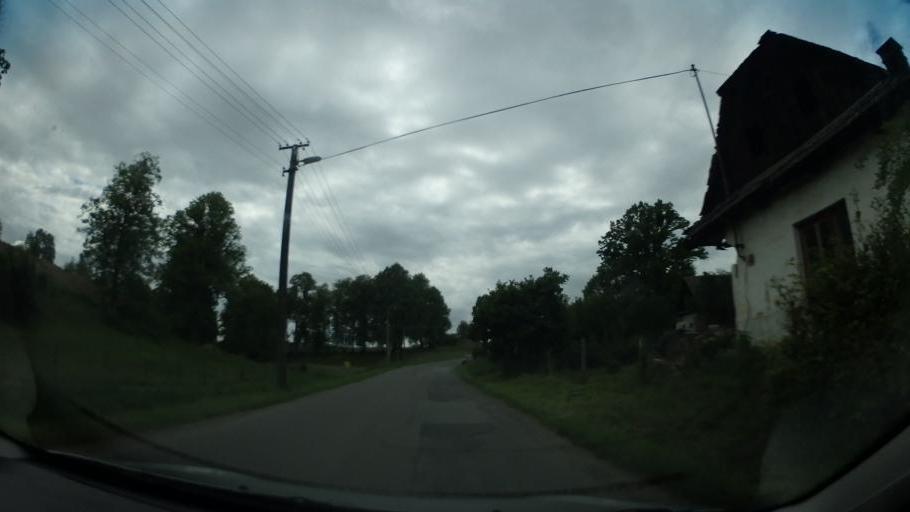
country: CZ
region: Pardubicky
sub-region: Okres Svitavy
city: Moravska Trebova
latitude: 49.8181
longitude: 16.6948
